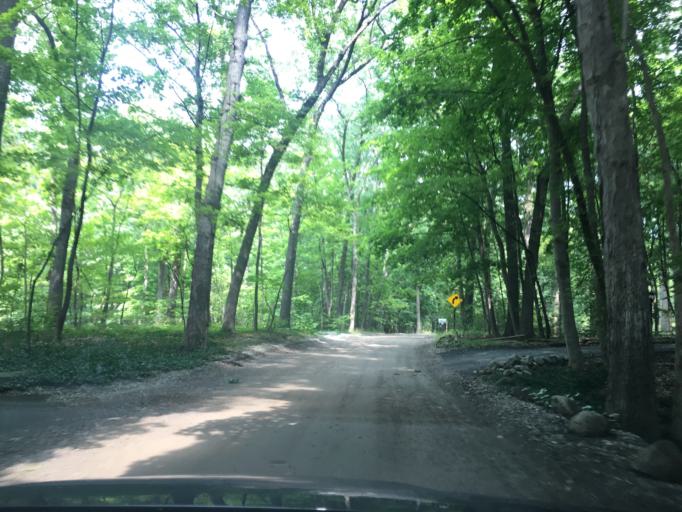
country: US
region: Michigan
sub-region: Oakland County
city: Bloomfield Hills
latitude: 42.5798
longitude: -83.2331
